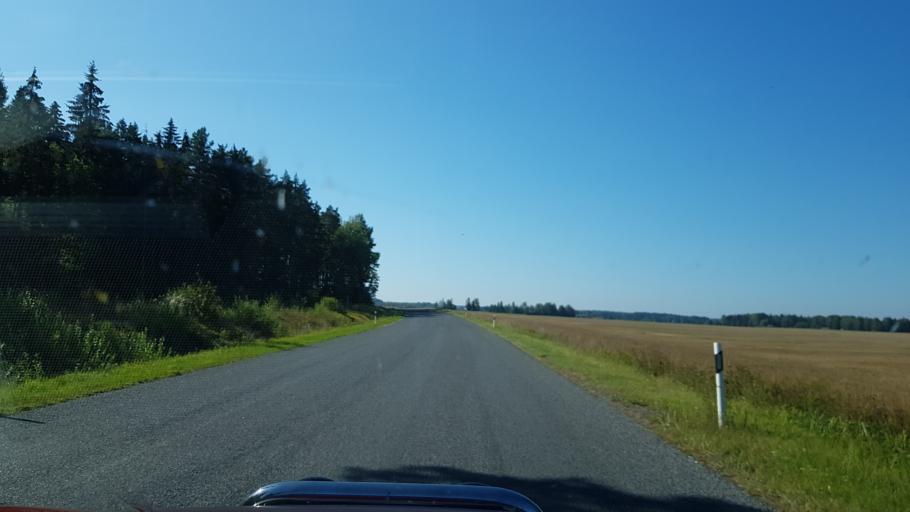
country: EE
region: Tartu
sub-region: UElenurme vald
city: Ulenurme
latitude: 58.3282
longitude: 26.8871
